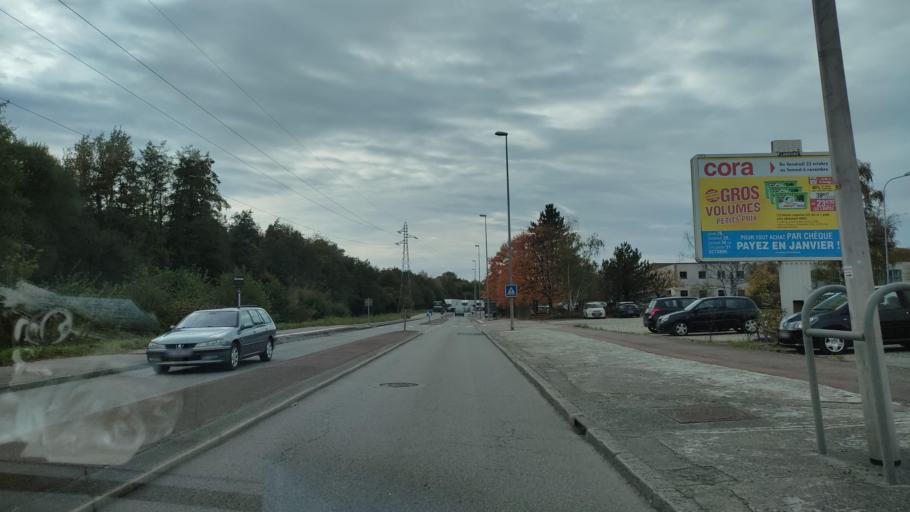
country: FR
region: Limousin
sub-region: Departement de la Haute-Vienne
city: Chaptelat
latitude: 45.8807
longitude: 1.2786
